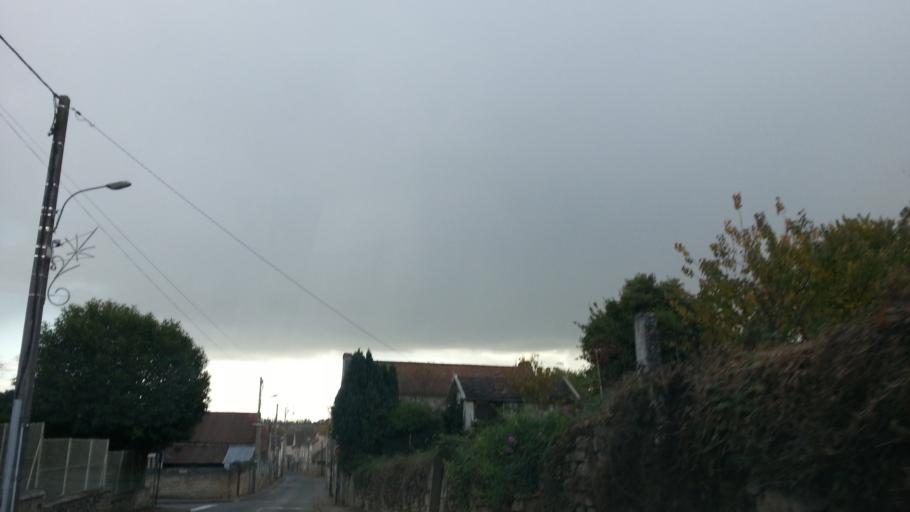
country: FR
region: Picardie
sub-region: Departement de l'Oise
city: Villers-sous-Saint-Leu
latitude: 49.2195
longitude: 2.4157
